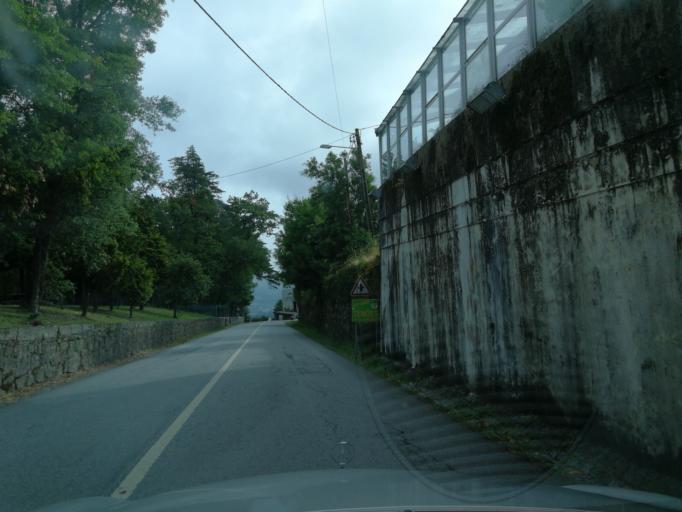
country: PT
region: Braga
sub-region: Braga
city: Adaufe
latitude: 41.5523
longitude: -8.3753
